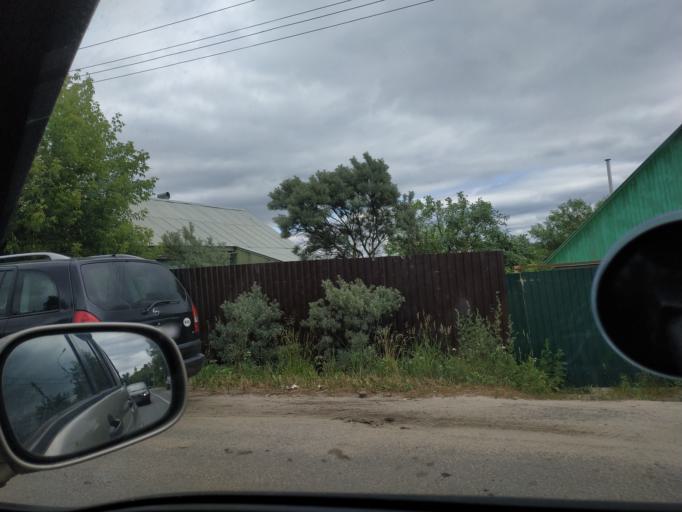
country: RU
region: Moskovskaya
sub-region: Shchelkovskiy Rayon
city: Grebnevo
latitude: 55.9930
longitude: 38.1280
